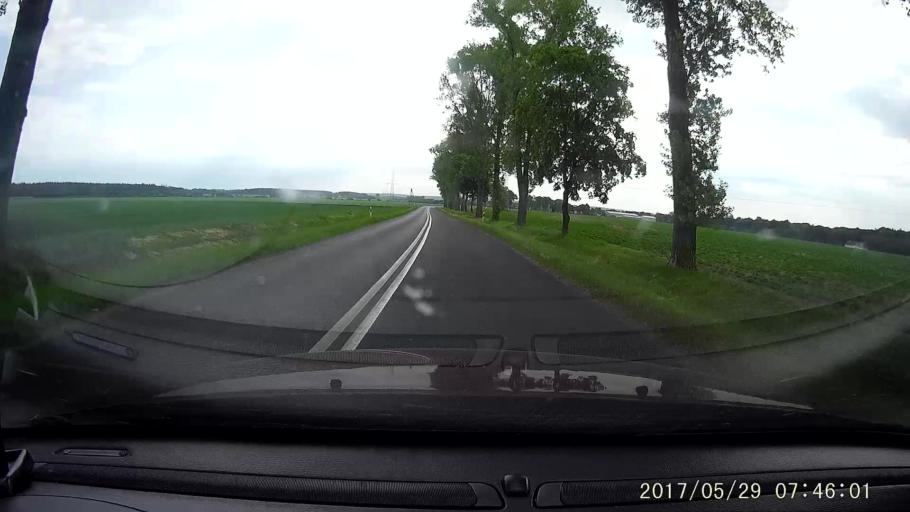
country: PL
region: Lower Silesian Voivodeship
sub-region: Powiat boleslawiecki
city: Boleslawiec
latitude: 51.2363
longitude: 15.6385
